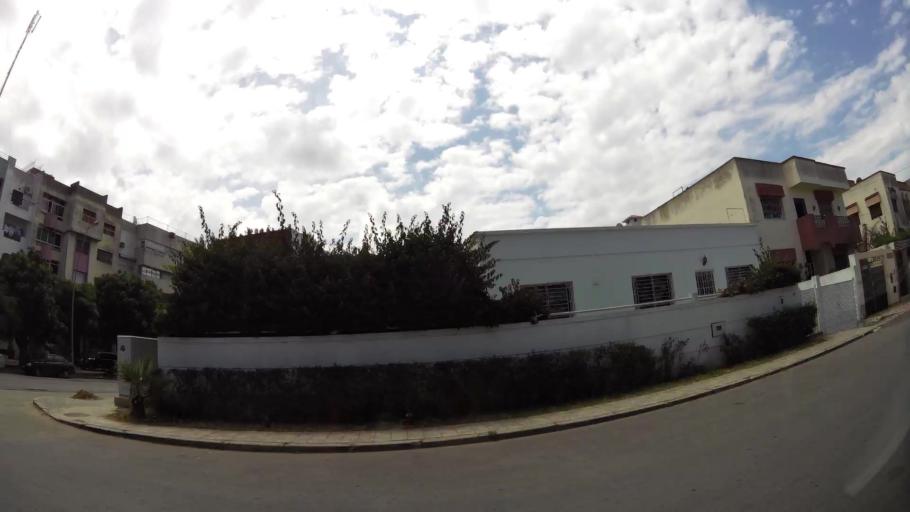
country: MA
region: Gharb-Chrarda-Beni Hssen
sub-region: Kenitra Province
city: Kenitra
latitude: 34.2567
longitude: -6.5976
